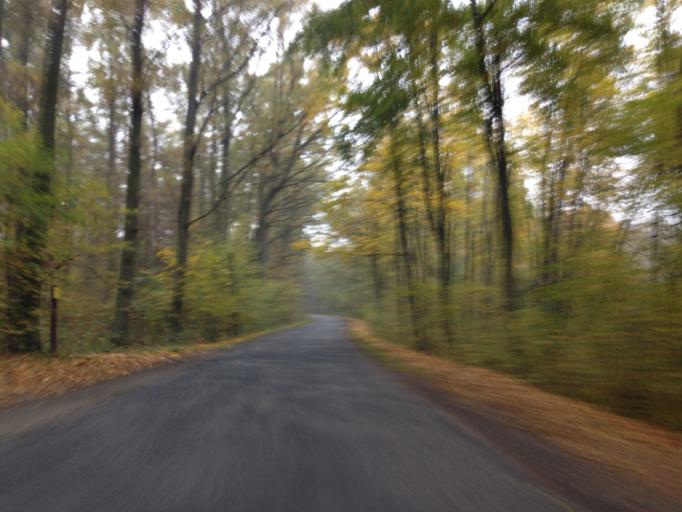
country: PL
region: Warmian-Masurian Voivodeship
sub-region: Powiat nowomiejski
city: Biskupiec
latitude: 53.4557
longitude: 19.3582
